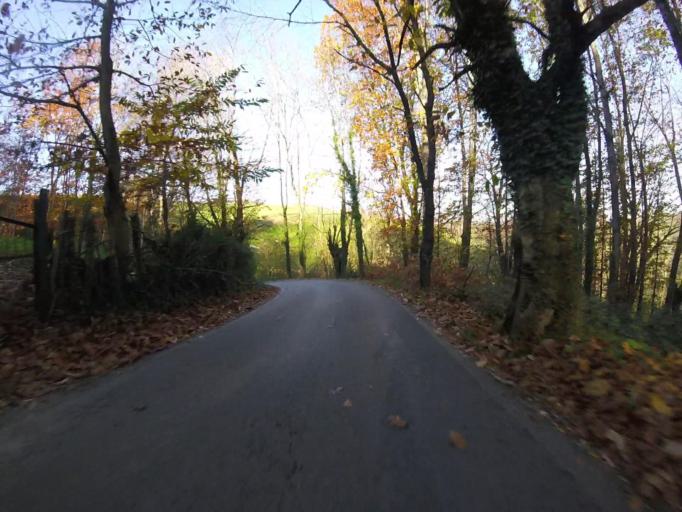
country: ES
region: Navarre
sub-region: Provincia de Navarra
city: Igantzi
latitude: 43.2324
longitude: -1.7020
